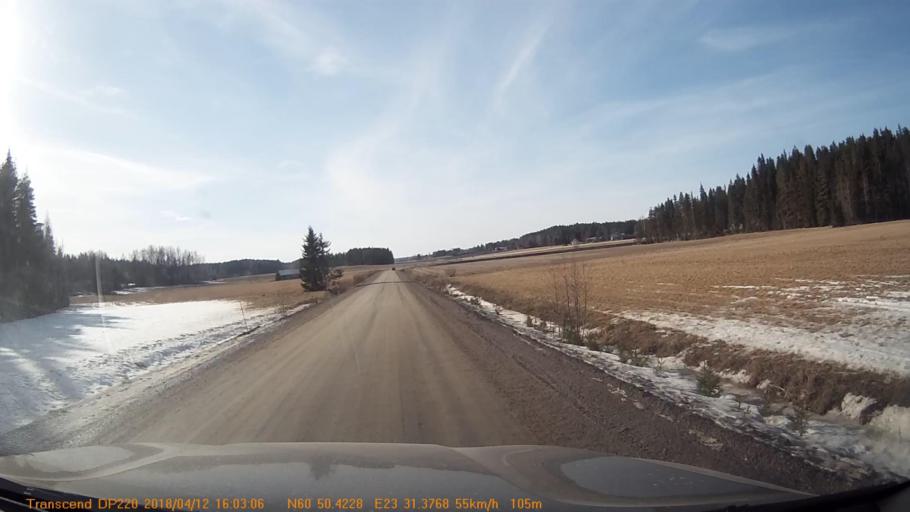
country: FI
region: Haeme
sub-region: Forssa
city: Jokioinen
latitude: 60.8404
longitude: 23.5227
